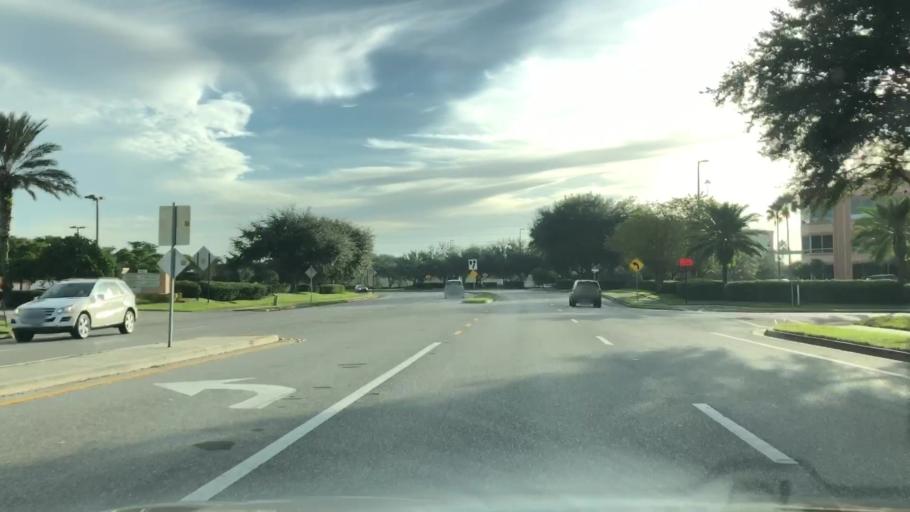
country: US
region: Florida
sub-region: Sarasota County
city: Fruitville
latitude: 27.3430
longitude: -82.4503
